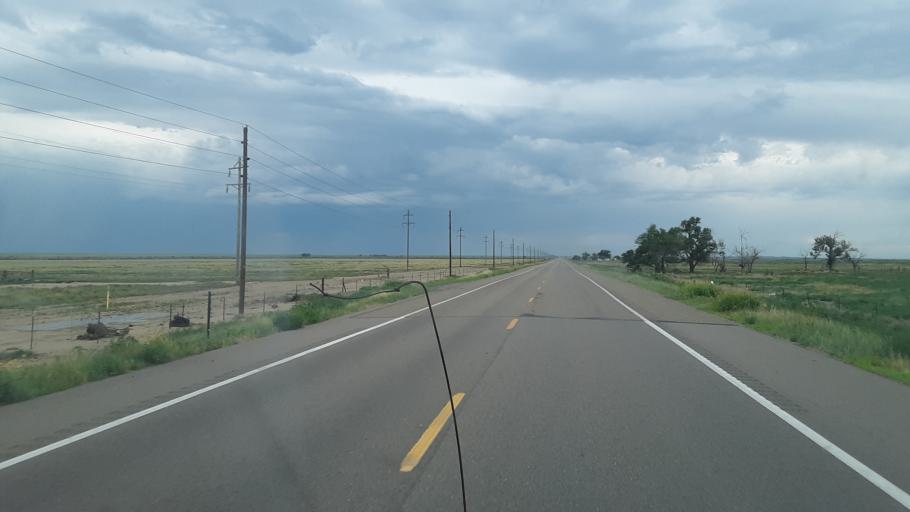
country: US
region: Colorado
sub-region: Crowley County
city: Ordway
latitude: 38.1950
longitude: -103.7484
